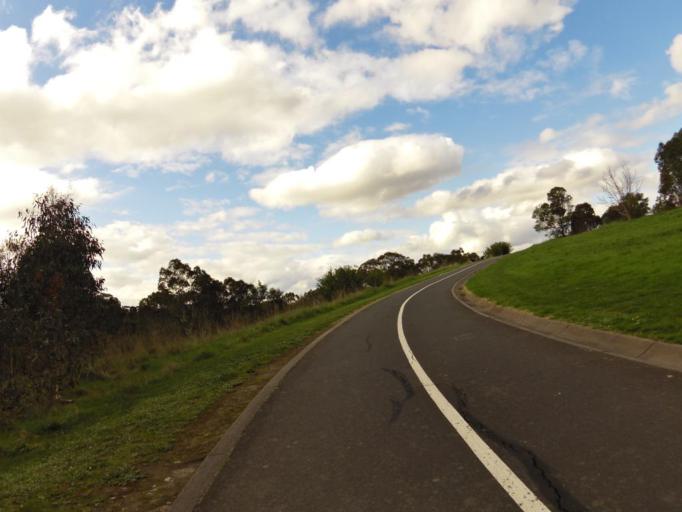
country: AU
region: Victoria
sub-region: Banyule
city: Darch
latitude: -37.7461
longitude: 145.1209
